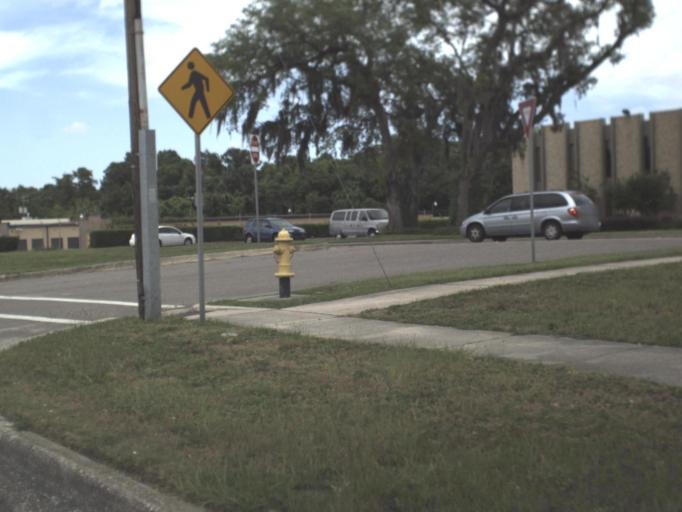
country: US
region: Florida
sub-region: Clay County
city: Bellair-Meadowbrook Terrace
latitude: 30.2613
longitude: -81.7403
